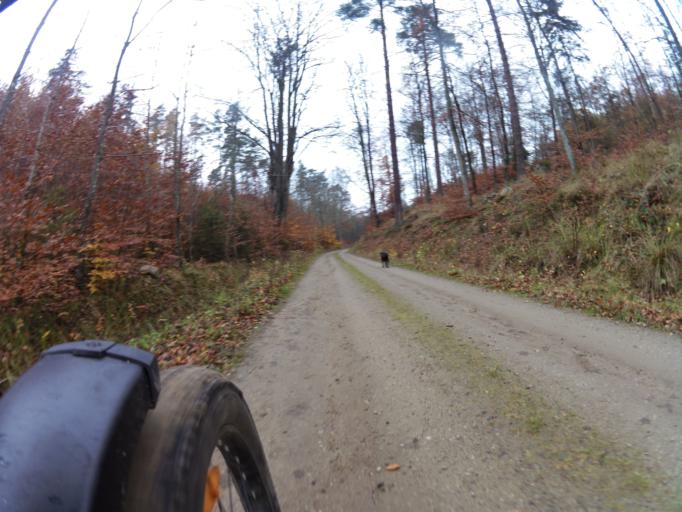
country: PL
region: Pomeranian Voivodeship
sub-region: Powiat pucki
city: Krokowa
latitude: 54.7136
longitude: 18.1416
